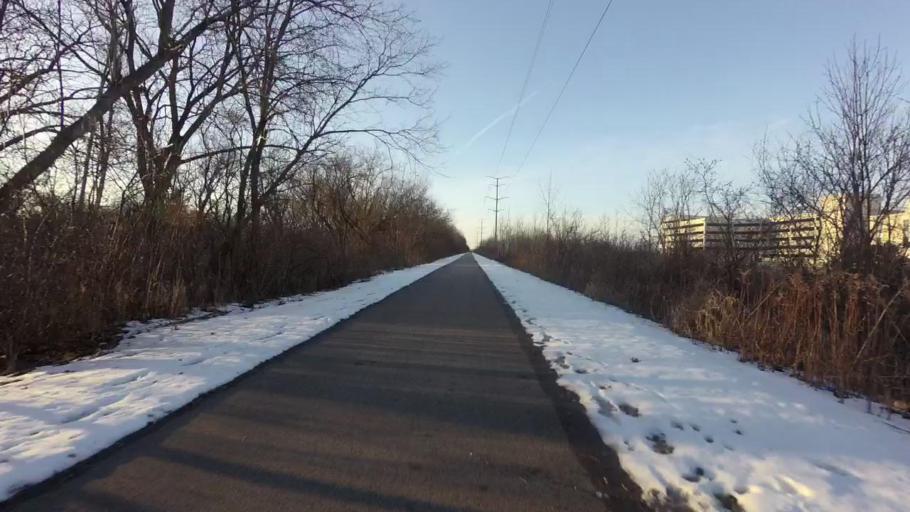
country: US
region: Wisconsin
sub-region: Milwaukee County
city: Glendale
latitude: 43.1238
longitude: -87.9388
